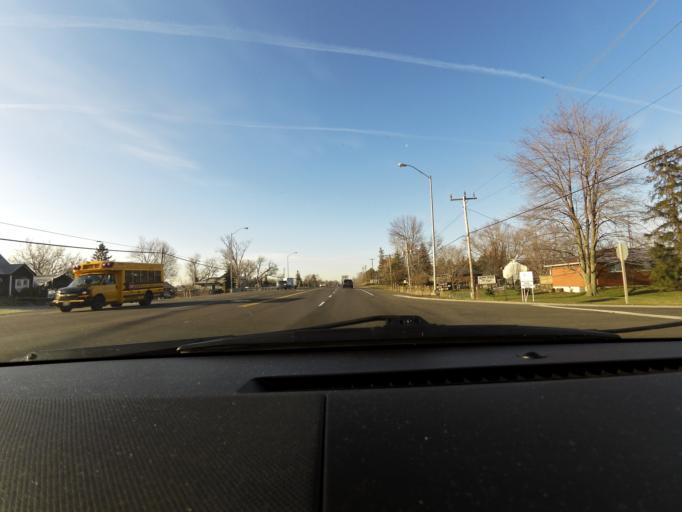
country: CA
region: Ontario
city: Ancaster
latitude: 43.1073
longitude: -79.9368
